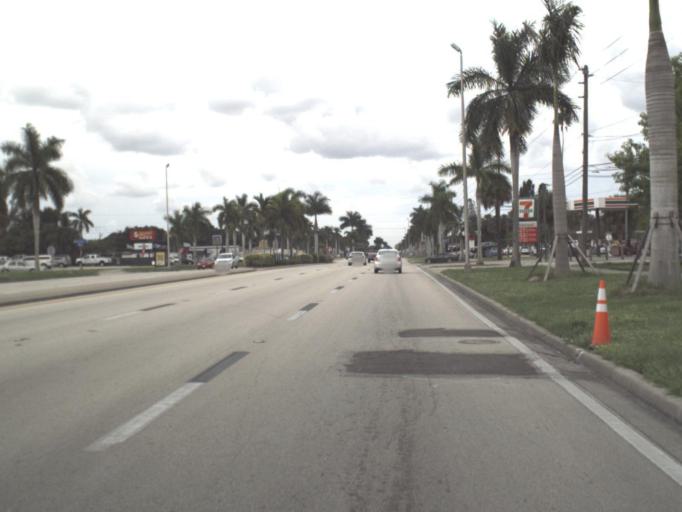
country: US
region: Florida
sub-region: Lee County
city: Tice
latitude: 26.6790
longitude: -81.8080
